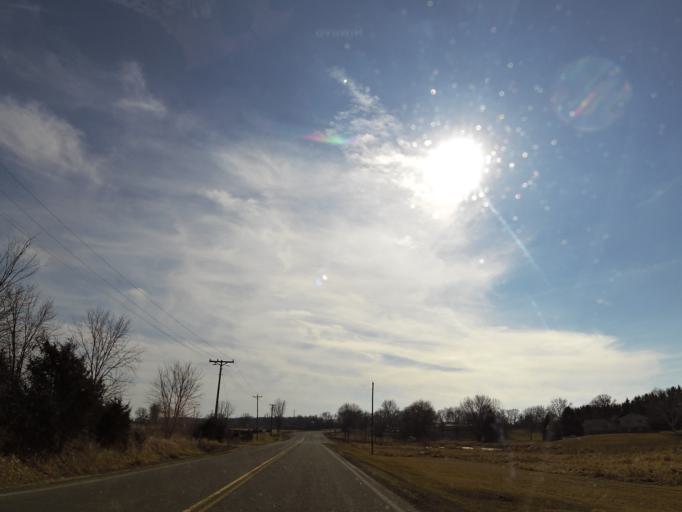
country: US
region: Minnesota
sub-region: Scott County
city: Prior Lake
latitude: 44.6552
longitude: -93.4670
